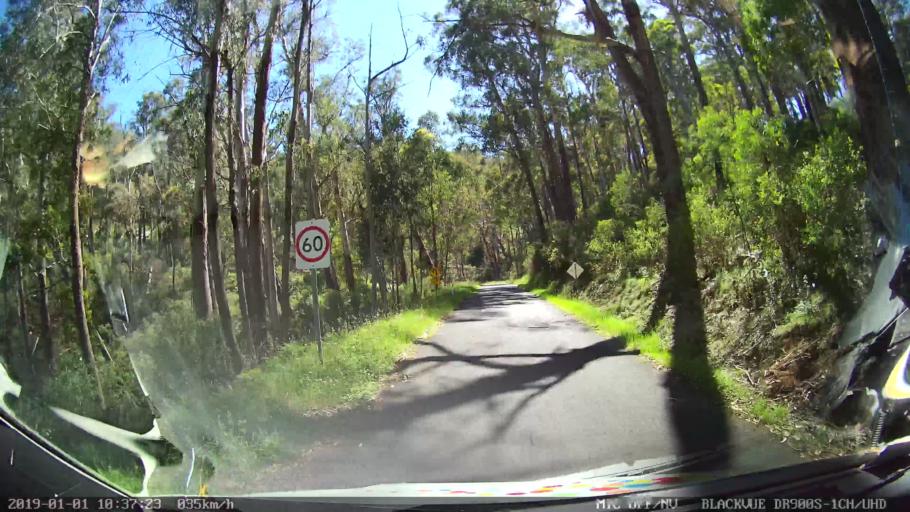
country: AU
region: New South Wales
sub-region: Snowy River
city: Jindabyne
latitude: -36.0489
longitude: 148.3038
